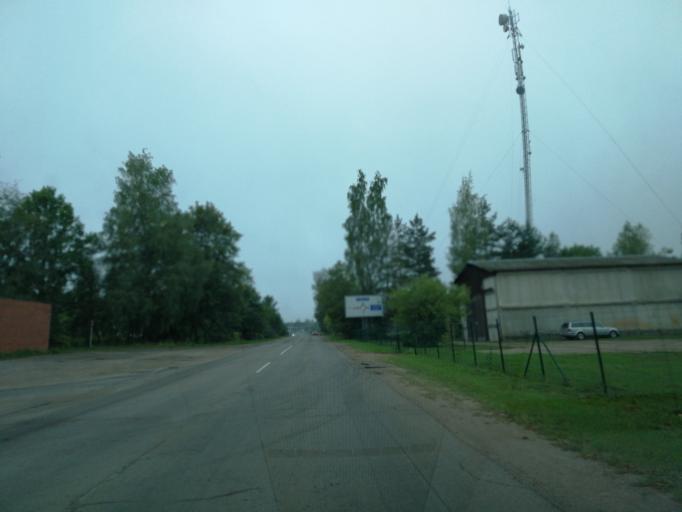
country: LV
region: Preilu Rajons
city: Preili
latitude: 56.3008
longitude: 26.7153
